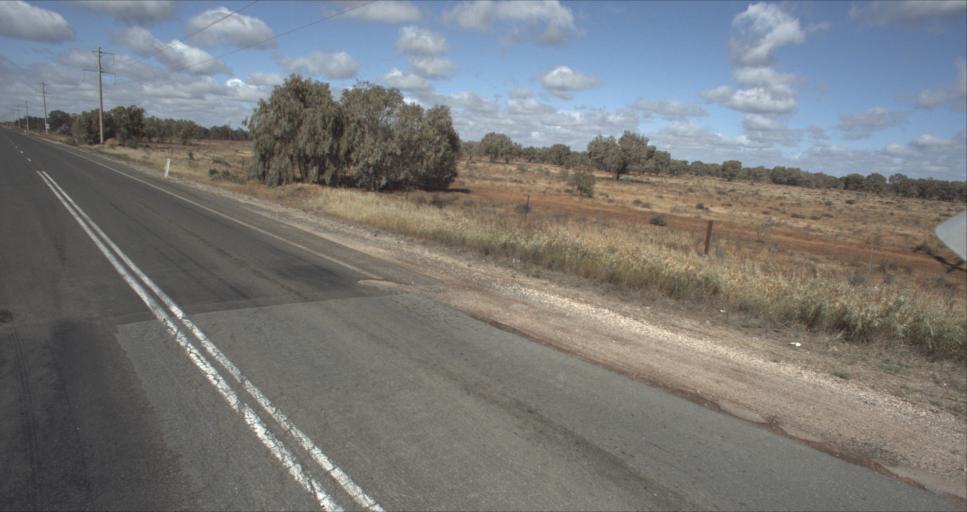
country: AU
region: New South Wales
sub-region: Murrumbidgee Shire
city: Darlington Point
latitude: -34.5171
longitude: 146.1764
